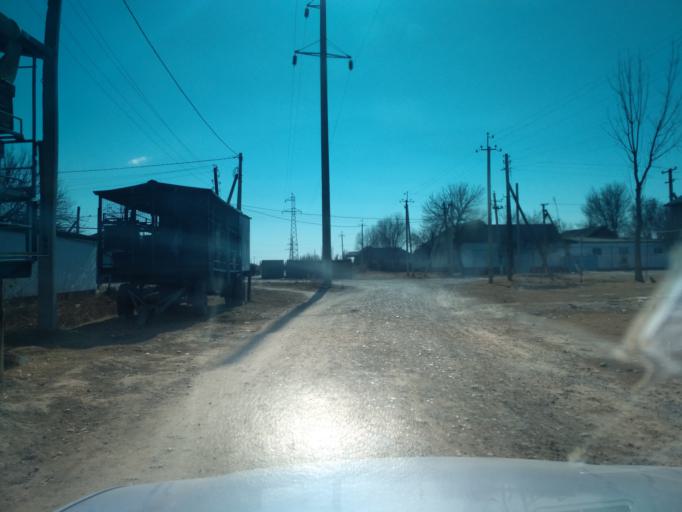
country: UZ
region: Sirdaryo
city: Guliston
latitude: 40.4869
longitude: 68.8120
